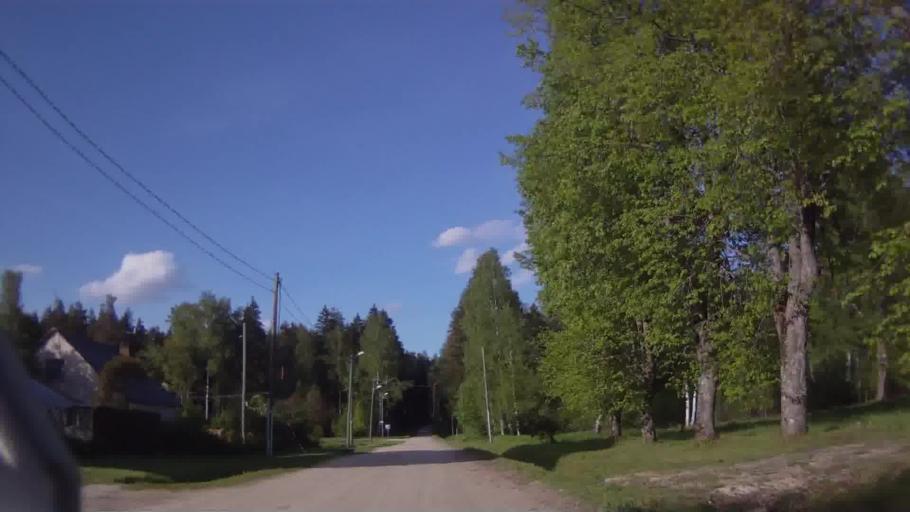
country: LV
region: Baldone
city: Baldone
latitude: 56.7469
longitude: 24.4108
